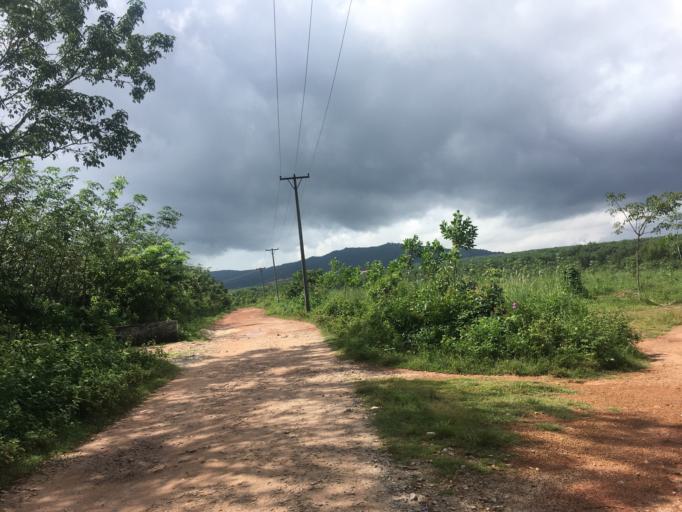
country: MM
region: Mon
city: Mawlamyine
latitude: 16.4622
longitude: 97.6900
